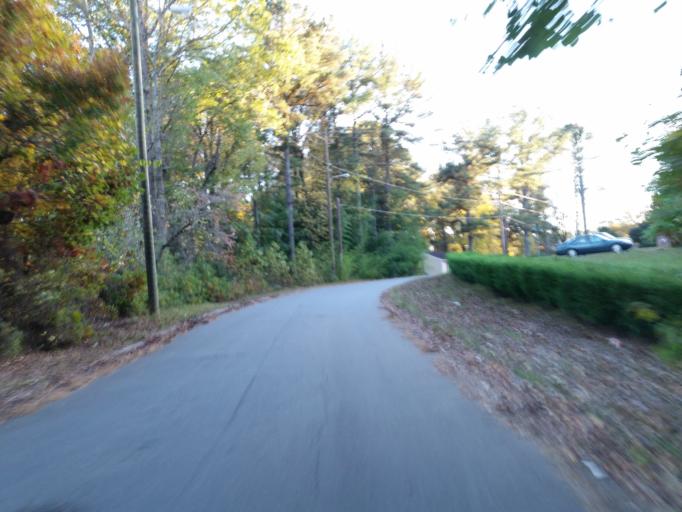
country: US
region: Georgia
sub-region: Cobb County
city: Marietta
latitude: 33.9570
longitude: -84.5258
